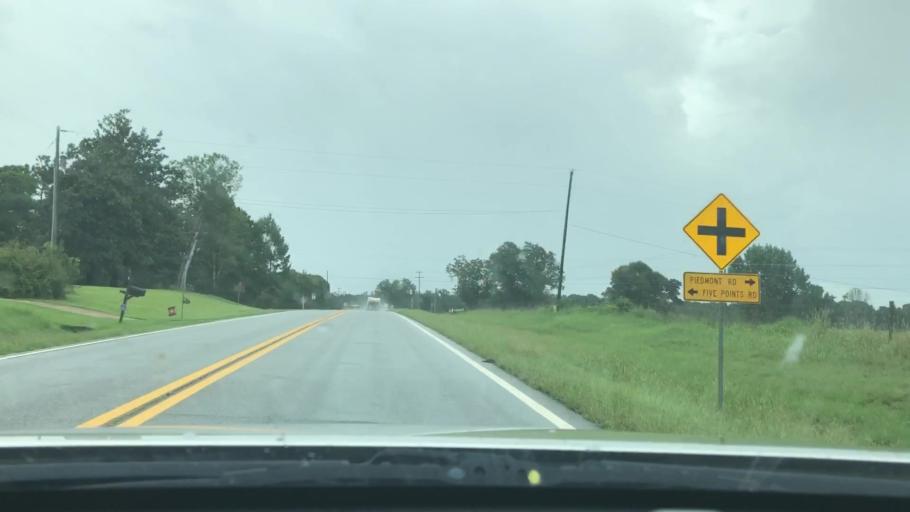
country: US
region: Georgia
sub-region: Lamar County
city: Barnesville
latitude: 33.0613
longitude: -84.2092
